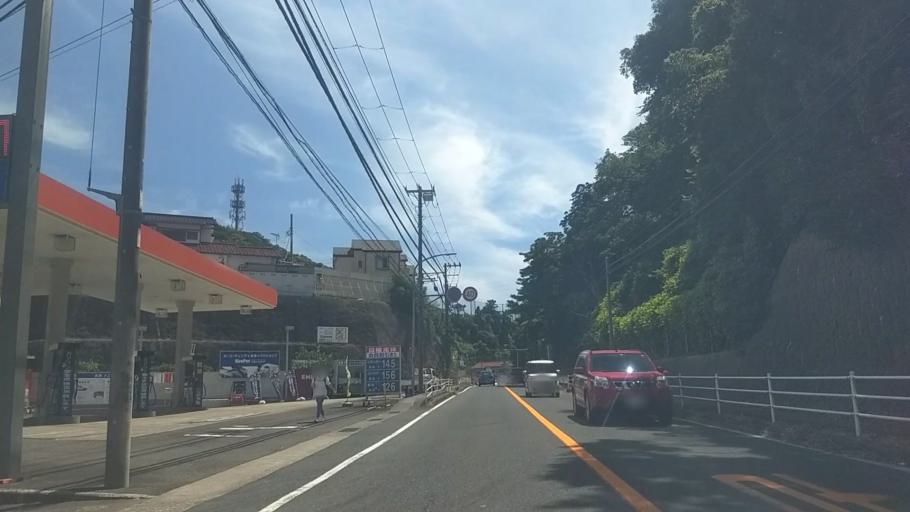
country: JP
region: Kanagawa
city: Yokosuka
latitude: 35.2484
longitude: 139.6651
